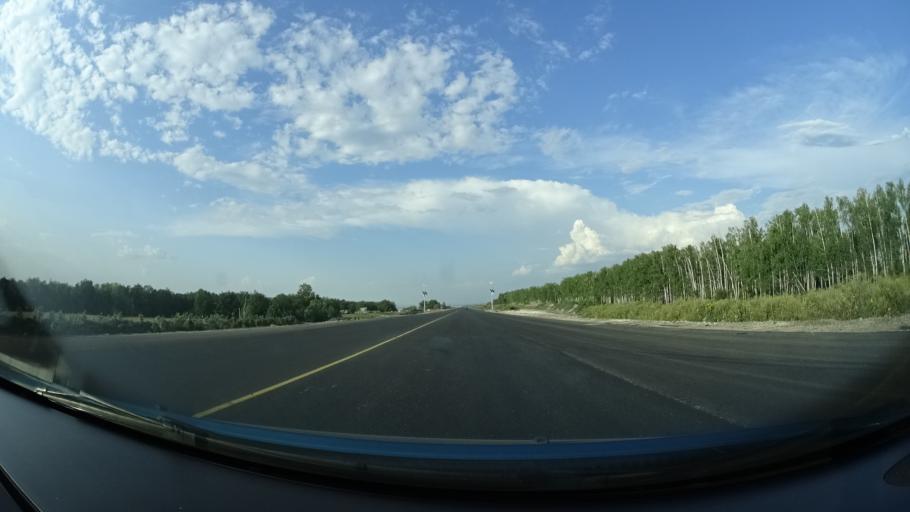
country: RU
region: Samara
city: Sukhodol
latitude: 53.7392
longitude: 50.8523
